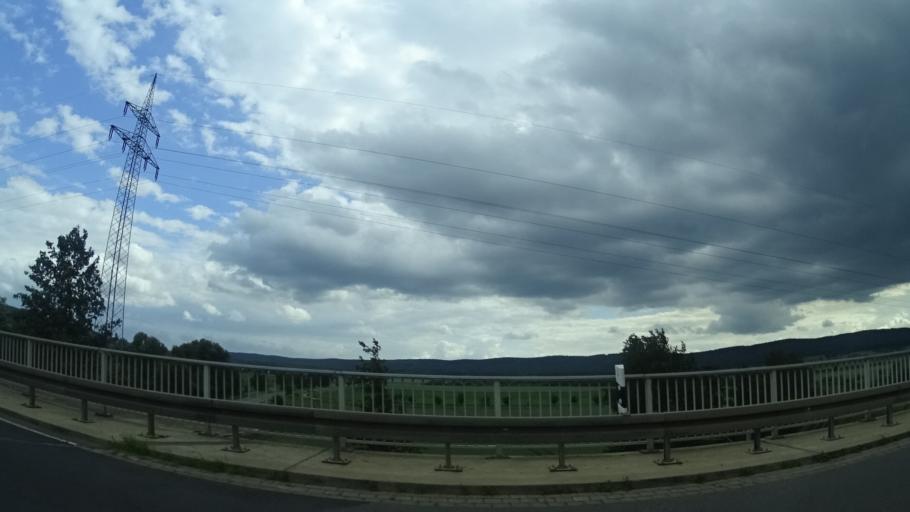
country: DE
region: Lower Saxony
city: Giesen
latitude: 52.1585
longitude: 9.8719
